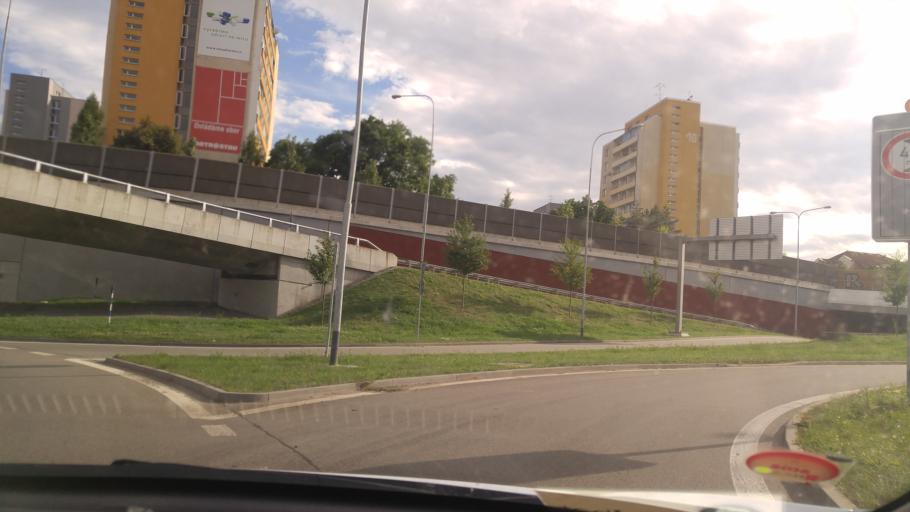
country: CZ
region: South Moravian
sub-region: Mesto Brno
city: Brno
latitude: 49.2174
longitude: 16.5847
